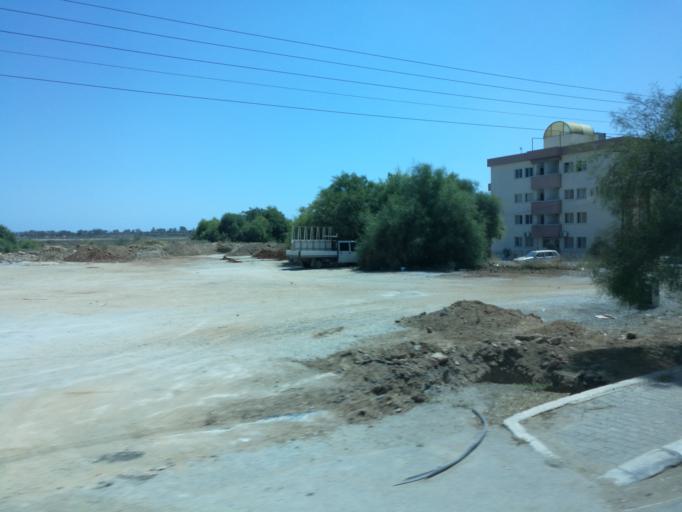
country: CY
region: Ammochostos
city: Famagusta
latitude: 35.1448
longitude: 33.9123
